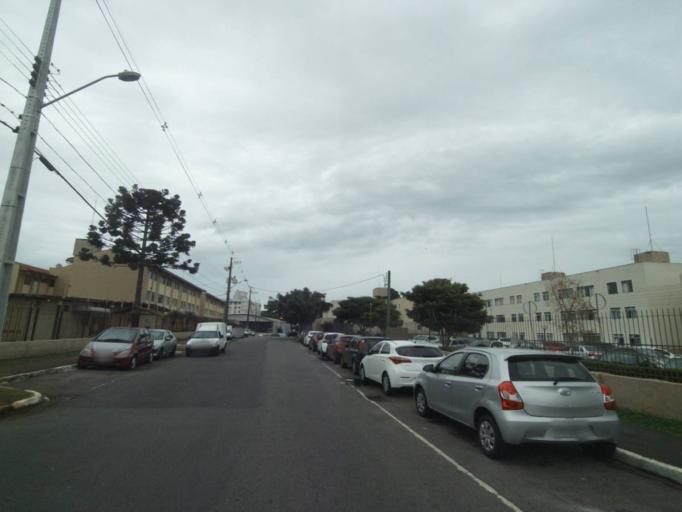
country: BR
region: Parana
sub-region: Curitiba
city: Curitiba
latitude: -25.4597
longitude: -49.3291
